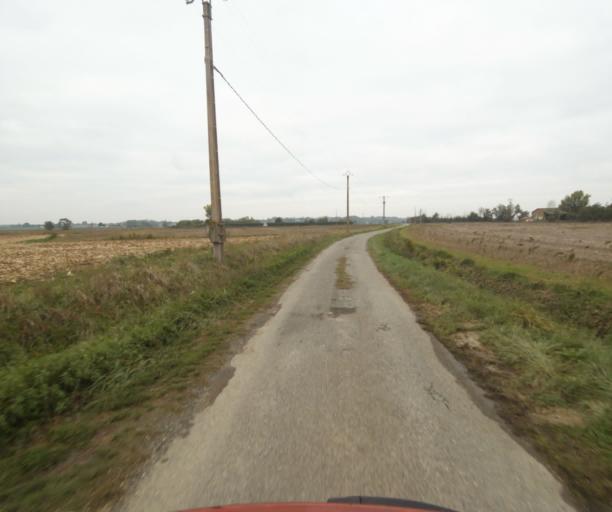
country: FR
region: Midi-Pyrenees
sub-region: Departement du Tarn-et-Garonne
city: Verdun-sur-Garonne
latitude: 43.8158
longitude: 1.2260
